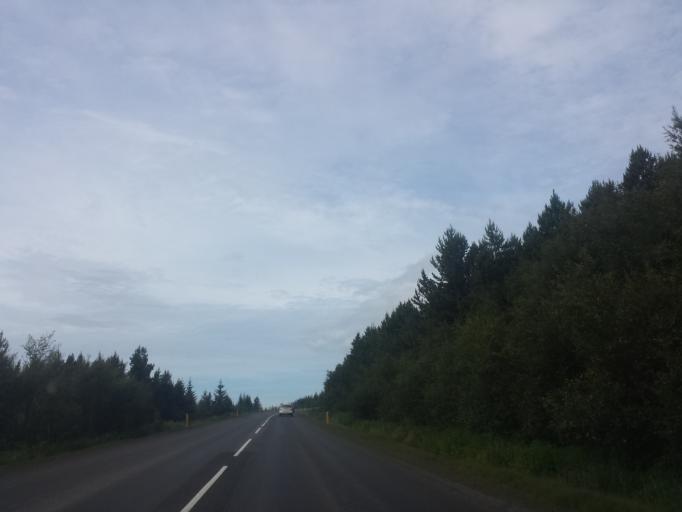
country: IS
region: Northeast
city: Akureyri
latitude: 65.6802
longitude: -18.0482
